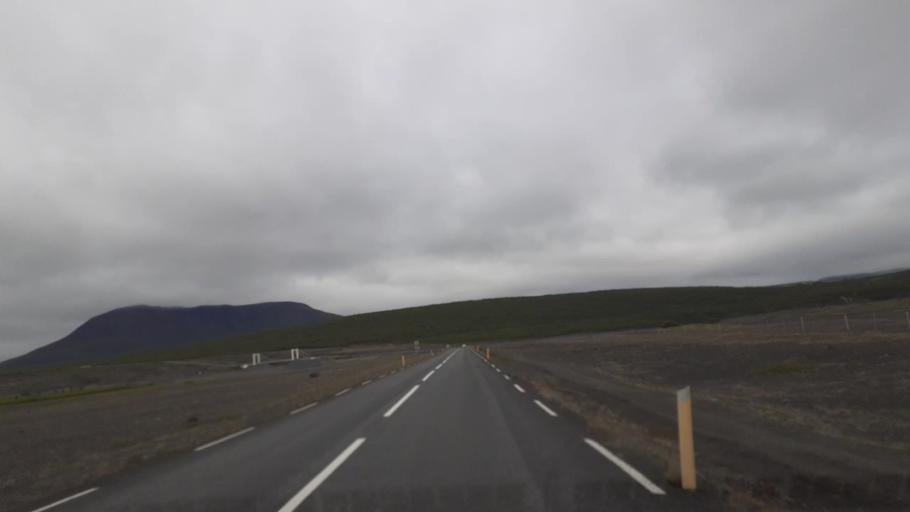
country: IS
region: Northeast
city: Husavik
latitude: 66.0307
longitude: -16.4604
